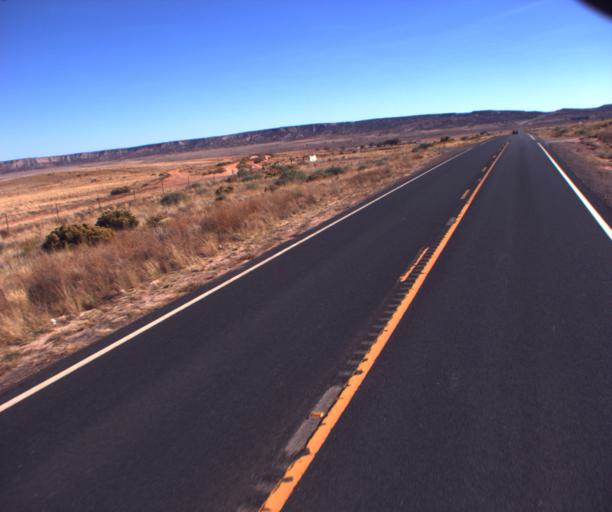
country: US
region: Arizona
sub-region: Apache County
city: Ganado
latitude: 35.7778
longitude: -109.6566
